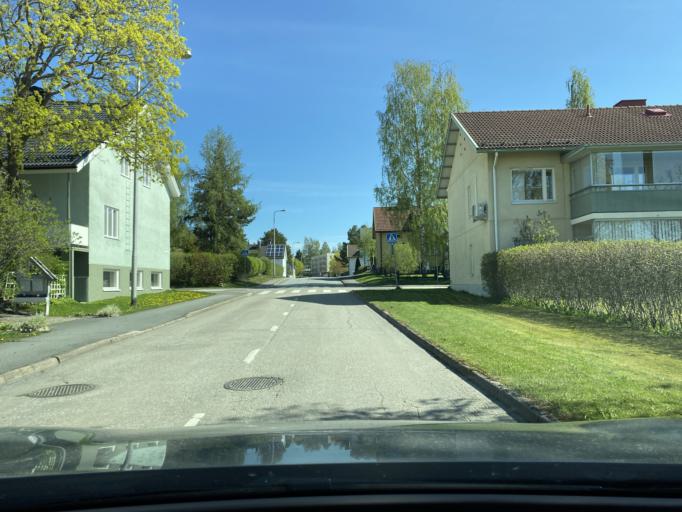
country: FI
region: Pirkanmaa
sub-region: Lounais-Pirkanmaa
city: Vammala
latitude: 61.3375
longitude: 22.9099
